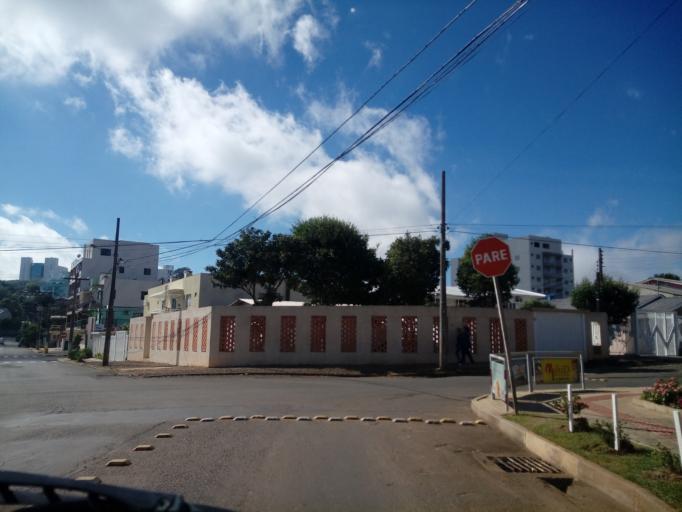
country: BR
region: Santa Catarina
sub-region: Chapeco
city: Chapeco
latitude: -27.1122
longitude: -52.6043
